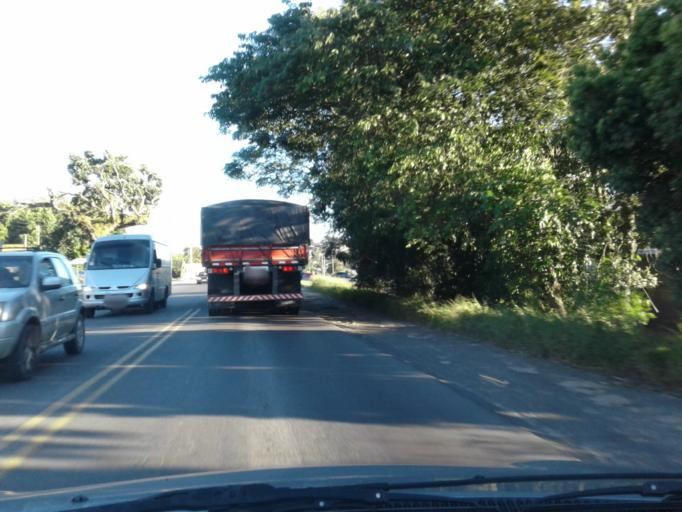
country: BR
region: Rio Grande do Sul
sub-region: Viamao
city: Viamao
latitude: -30.0797
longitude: -51.0172
